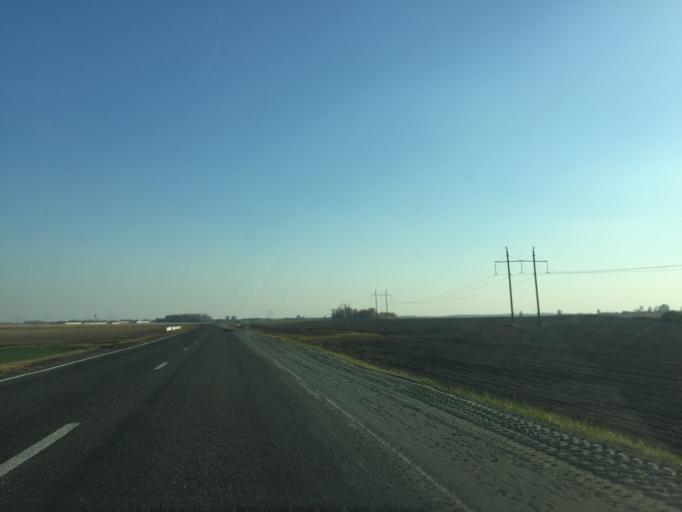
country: BY
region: Gomel
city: Dobrush
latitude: 52.3269
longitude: 31.2424
